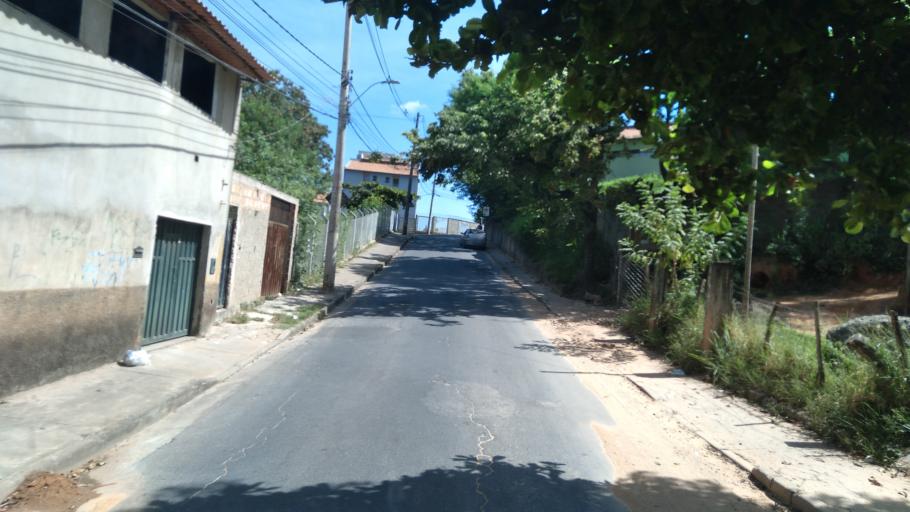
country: BR
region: Minas Gerais
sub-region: Belo Horizonte
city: Belo Horizonte
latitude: -19.8457
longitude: -43.9004
